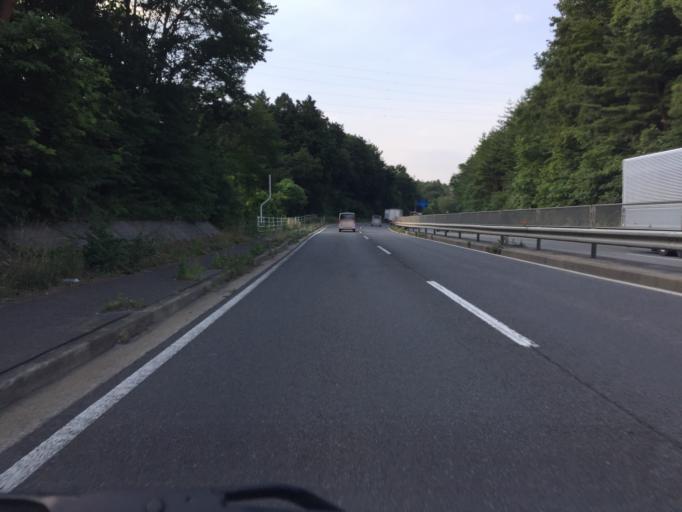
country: JP
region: Fukushima
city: Fukushima-shi
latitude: 37.7070
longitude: 140.4633
